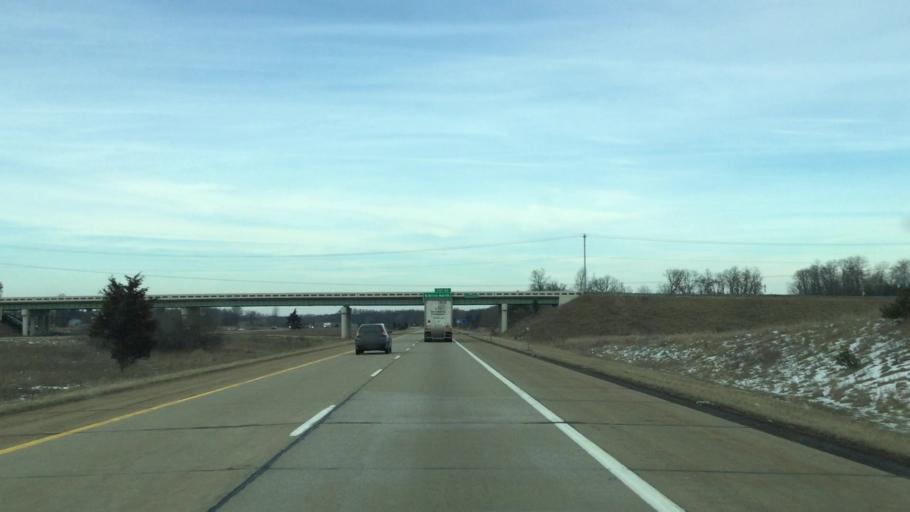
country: US
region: Michigan
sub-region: Calhoun County
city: Marshall
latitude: 42.3315
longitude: -84.9877
